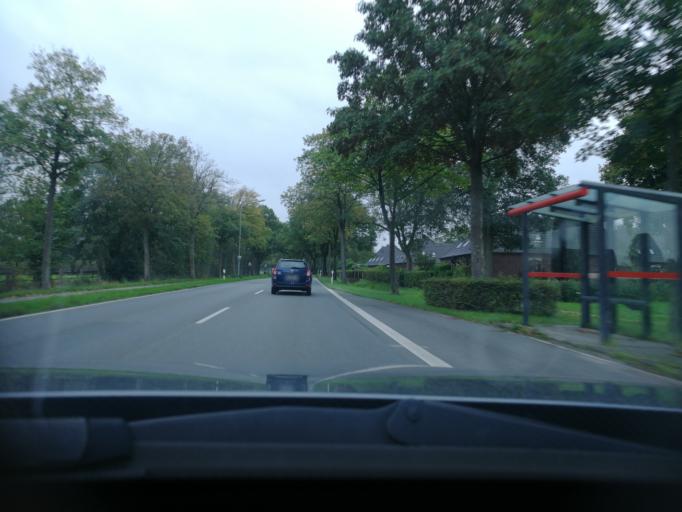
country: DE
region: North Rhine-Westphalia
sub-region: Regierungsbezirk Dusseldorf
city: Kevelaer
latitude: 51.5296
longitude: 6.2426
